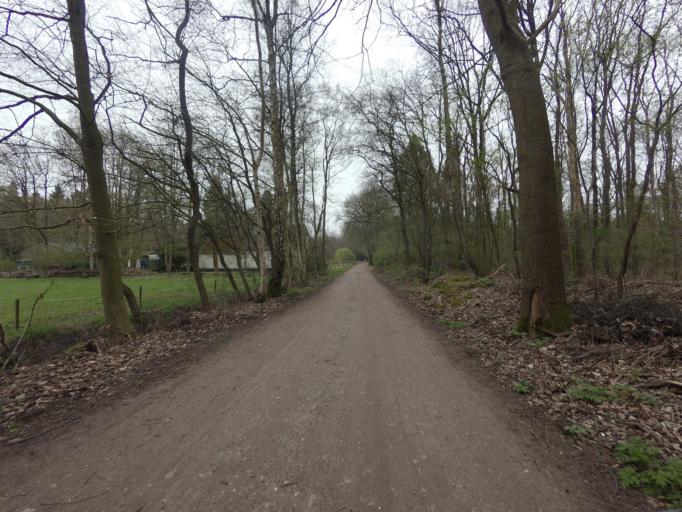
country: NL
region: Utrecht
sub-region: Gemeente Soest
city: Soest
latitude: 52.1639
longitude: 5.2552
